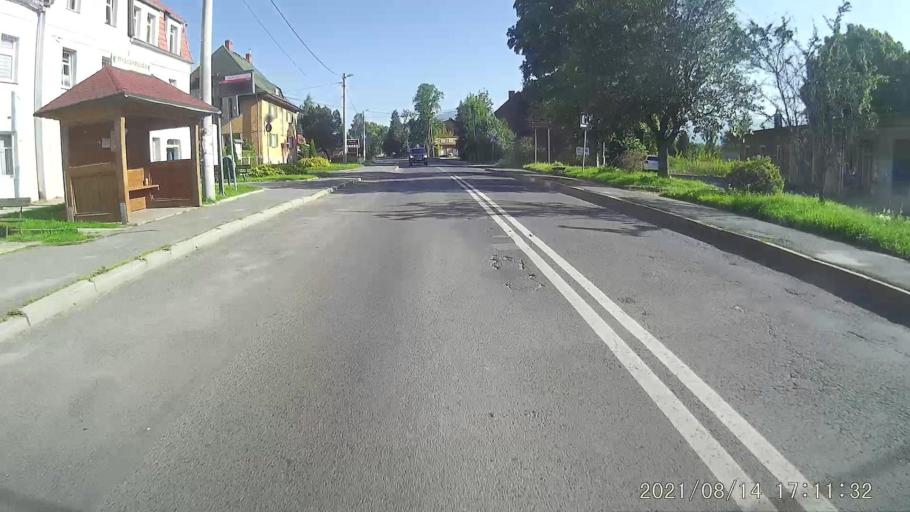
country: PL
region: Lower Silesian Voivodeship
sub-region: Powiat jeleniogorski
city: Myslakowice
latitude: 50.8355
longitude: 15.7886
